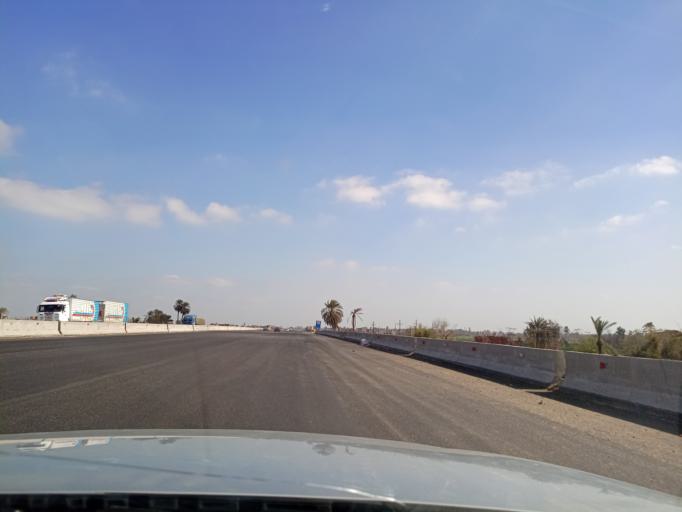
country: EG
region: Muhafazat al Minufiyah
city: Al Bajur
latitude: 30.4115
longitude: 31.0589
